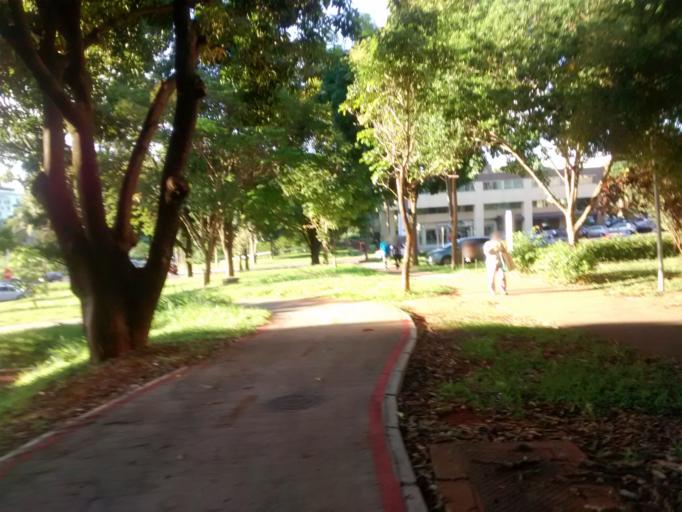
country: BR
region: Federal District
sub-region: Brasilia
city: Brasilia
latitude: -15.7484
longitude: -47.8846
